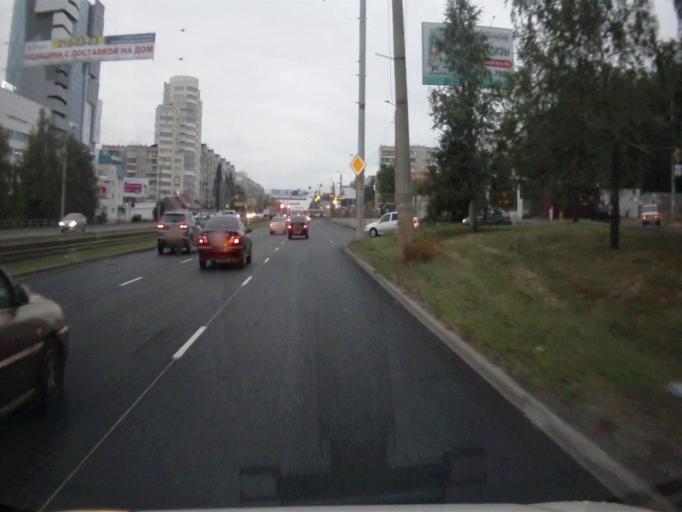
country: RU
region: Chelyabinsk
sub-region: Gorod Chelyabinsk
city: Chelyabinsk
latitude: 55.1891
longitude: 61.3366
